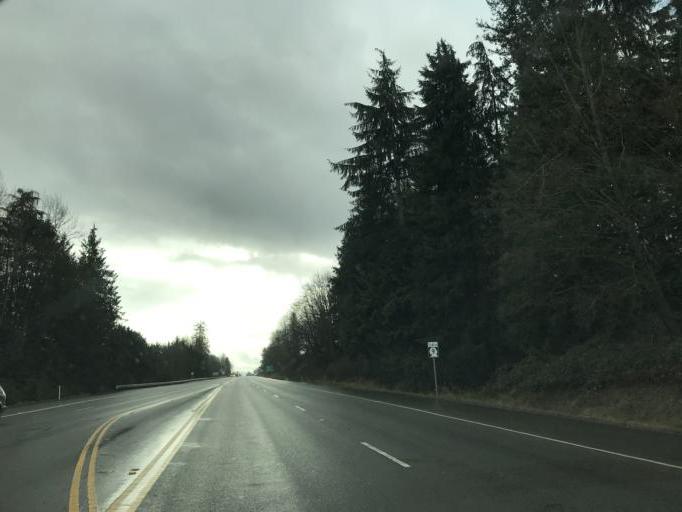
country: US
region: Washington
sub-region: Snohomish County
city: West Lake Stevens
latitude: 48.0122
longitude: -122.1087
